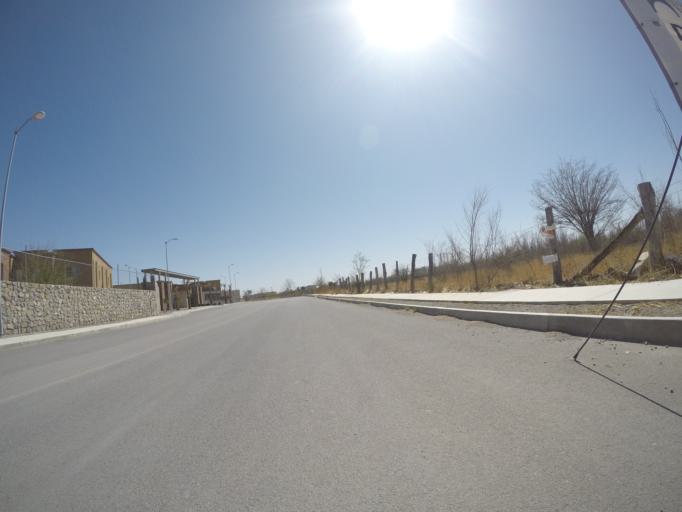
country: MX
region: Chihuahua
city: Ciudad Juarez
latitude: 31.6935
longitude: -106.4140
